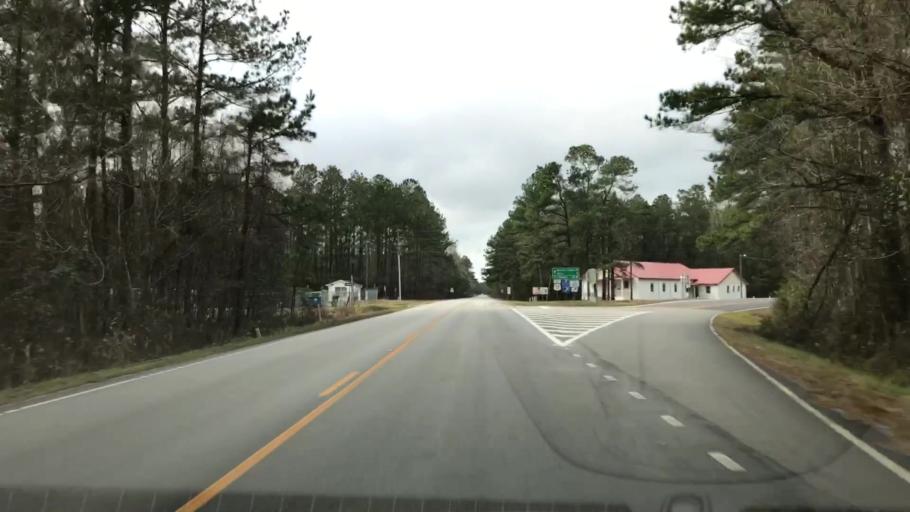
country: US
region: South Carolina
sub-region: Berkeley County
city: Saint Stephen
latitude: 33.2866
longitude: -79.7565
